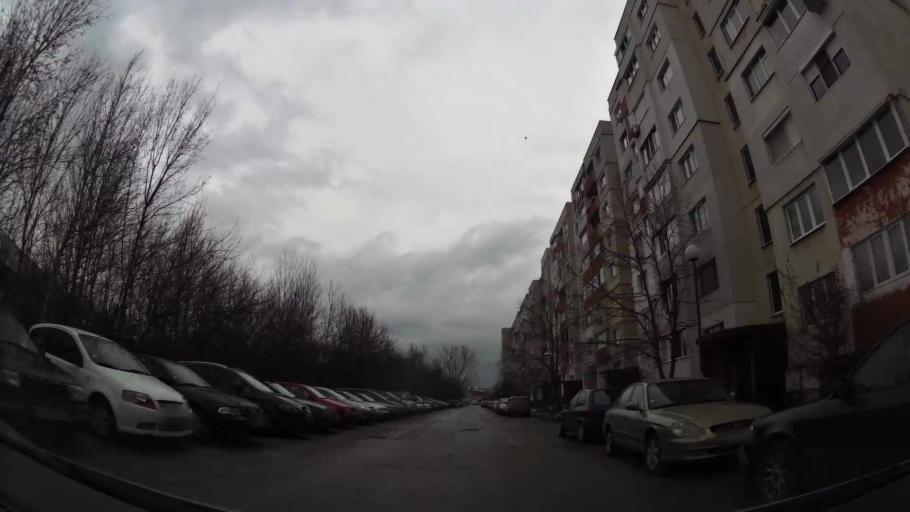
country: BG
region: Sofia-Capital
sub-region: Stolichna Obshtina
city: Sofia
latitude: 42.7393
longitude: 23.2723
